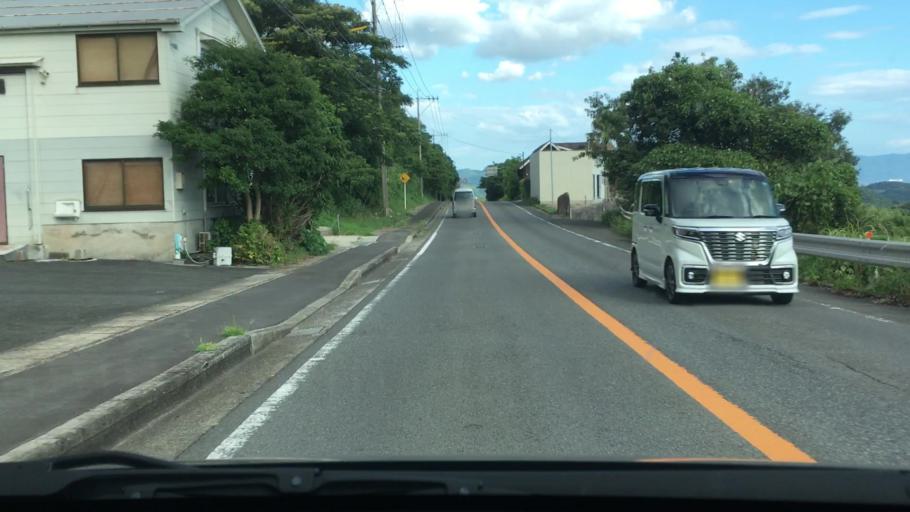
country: JP
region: Nagasaki
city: Togitsu
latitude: 32.8225
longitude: 129.7253
